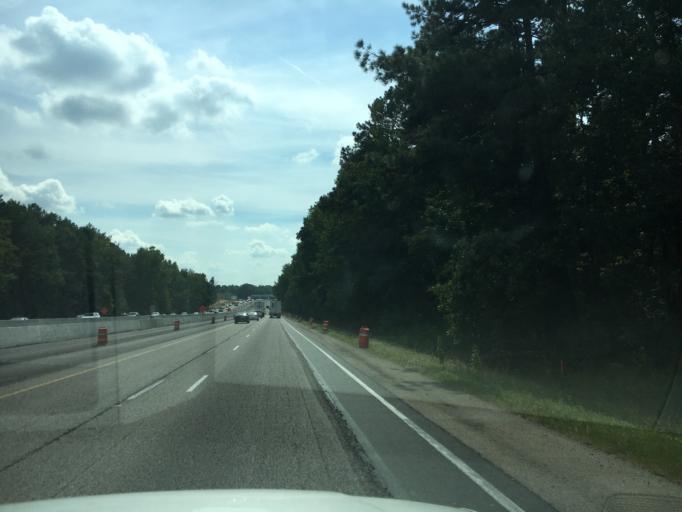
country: US
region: Georgia
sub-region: Gwinnett County
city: Buford
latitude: 34.0680
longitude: -83.9353
